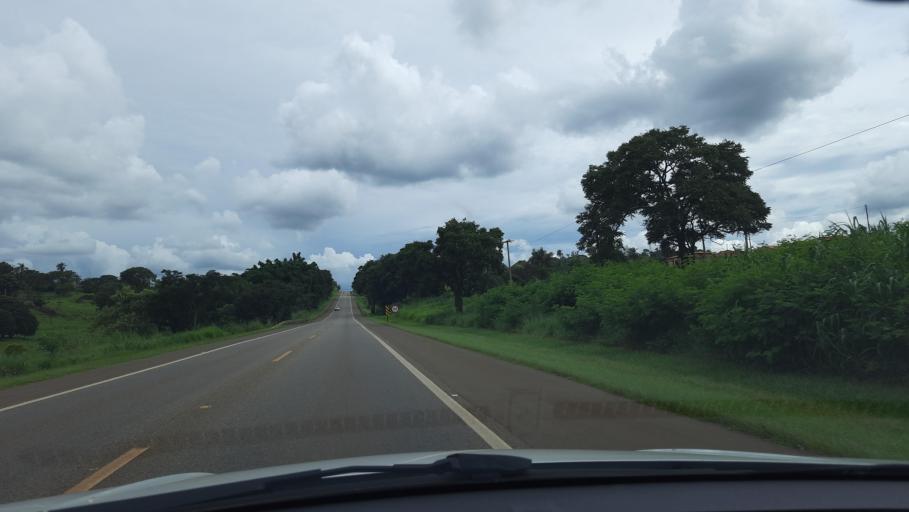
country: BR
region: Sao Paulo
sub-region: Sao Joao Da Boa Vista
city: Sao Joao da Boa Vista
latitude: -21.9355
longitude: -46.8471
